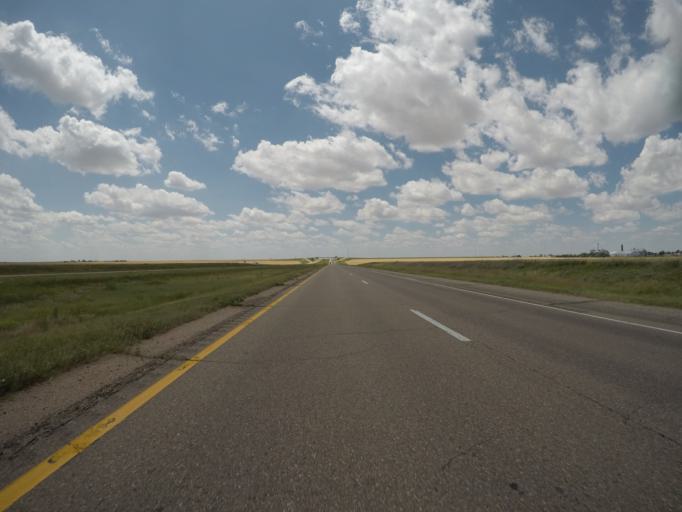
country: US
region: Colorado
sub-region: Kit Carson County
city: Burlington
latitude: 39.2942
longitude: -102.4161
